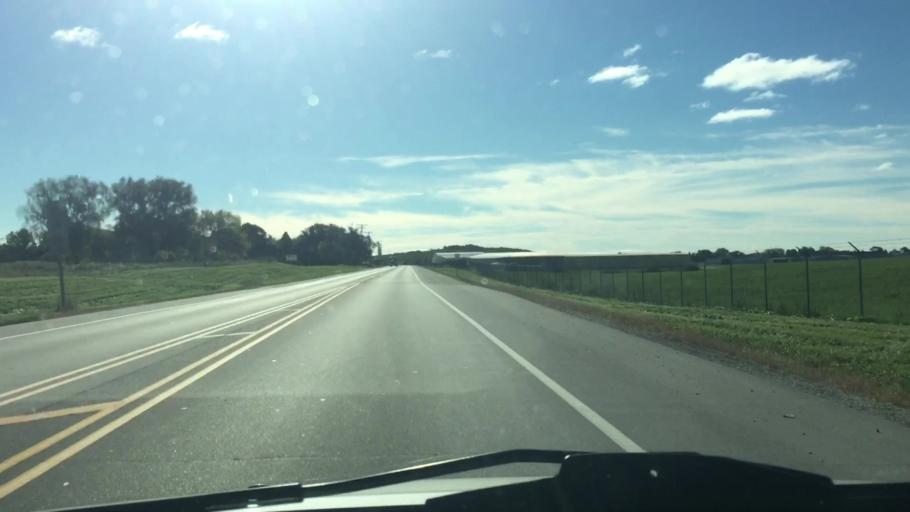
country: US
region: Wisconsin
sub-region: Waukesha County
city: Waukesha
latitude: 43.0460
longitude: -88.2338
